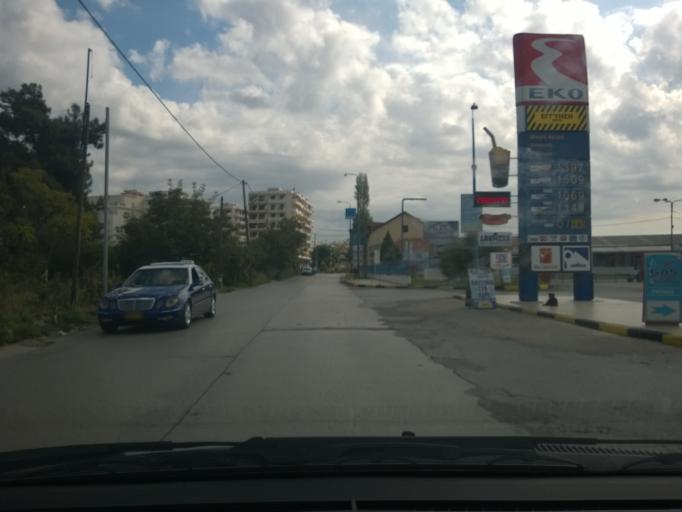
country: GR
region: Central Macedonia
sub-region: Nomos Thessalonikis
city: Menemeni
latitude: 40.6533
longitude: 22.9053
